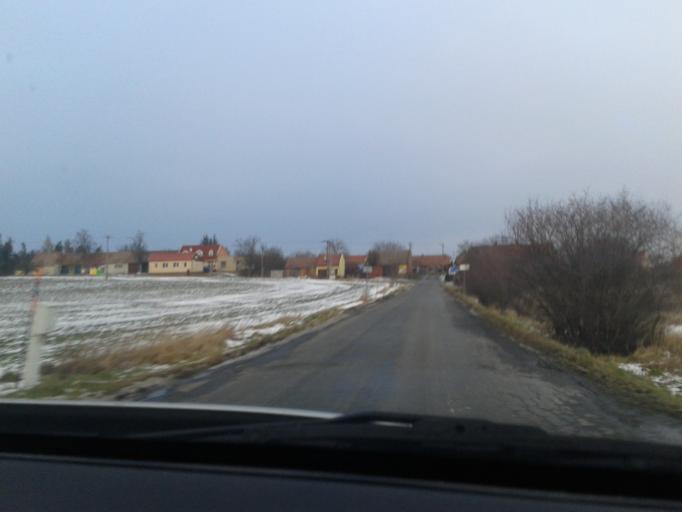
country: CZ
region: Olomoucky
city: Pteni
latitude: 49.5009
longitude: 16.9434
